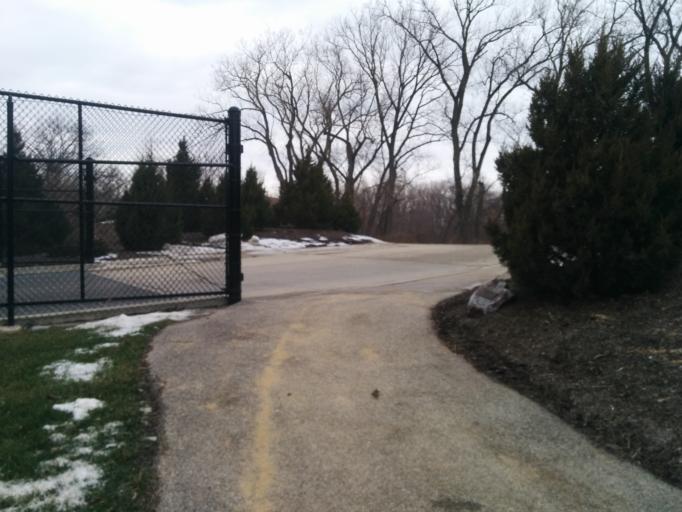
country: US
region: Illinois
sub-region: Cook County
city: Glencoe
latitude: 42.1380
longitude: -87.7816
